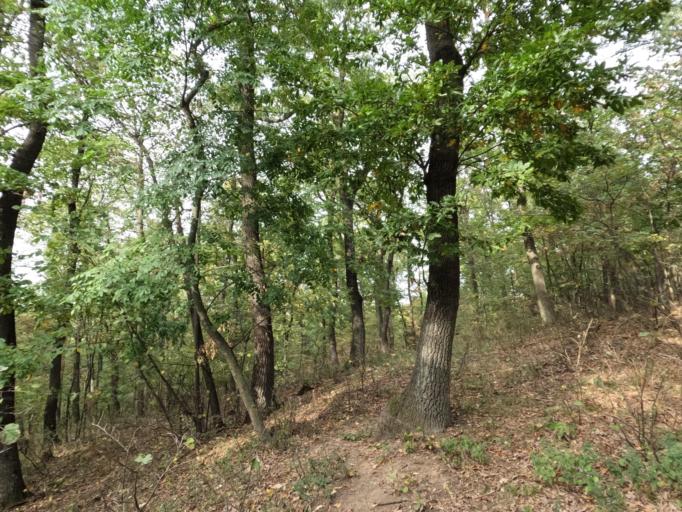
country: HU
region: Tolna
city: Szentgalpuszta
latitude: 46.3201
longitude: 18.6494
